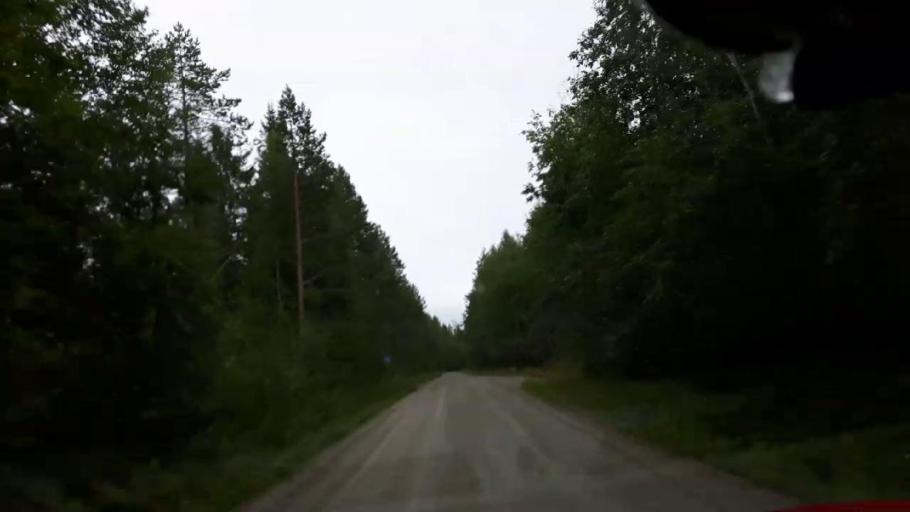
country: SE
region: Vaesternorrland
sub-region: Ange Kommun
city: Ange
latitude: 62.8031
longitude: 15.7629
